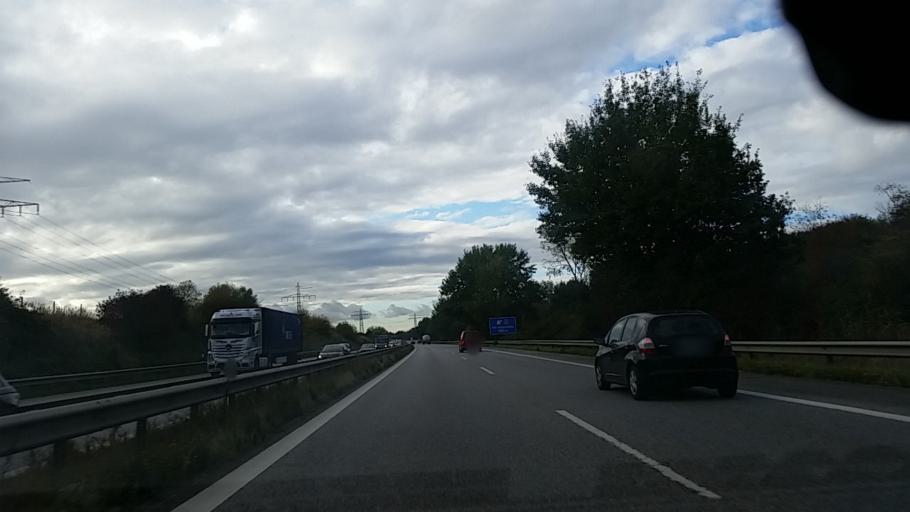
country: DE
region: Schleswig-Holstein
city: Oststeinbek
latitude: 53.4843
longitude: 10.1331
